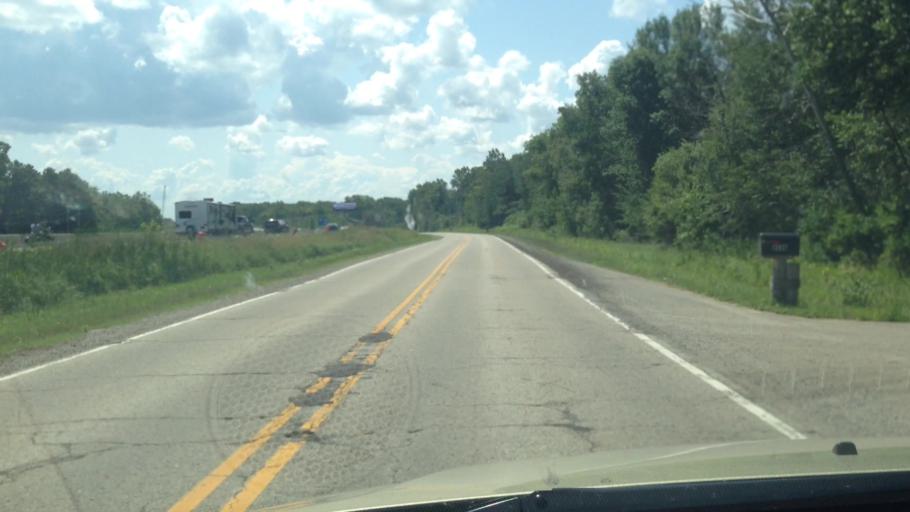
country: US
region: Wisconsin
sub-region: Brown County
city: Suamico
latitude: 44.6490
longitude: -88.0505
